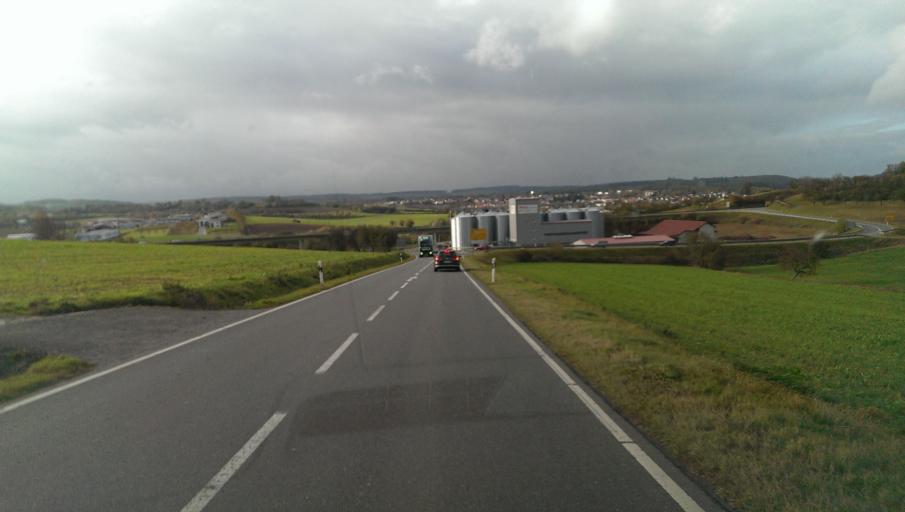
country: DE
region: Baden-Wuerttemberg
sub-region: Karlsruhe Region
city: Buchen
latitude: 49.5103
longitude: 9.3348
